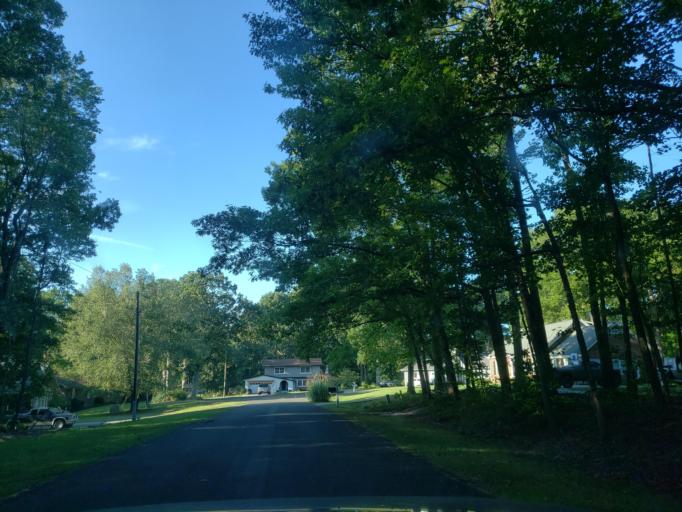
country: US
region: North Carolina
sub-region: Vance County
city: Henderson
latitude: 36.4058
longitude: -78.3809
